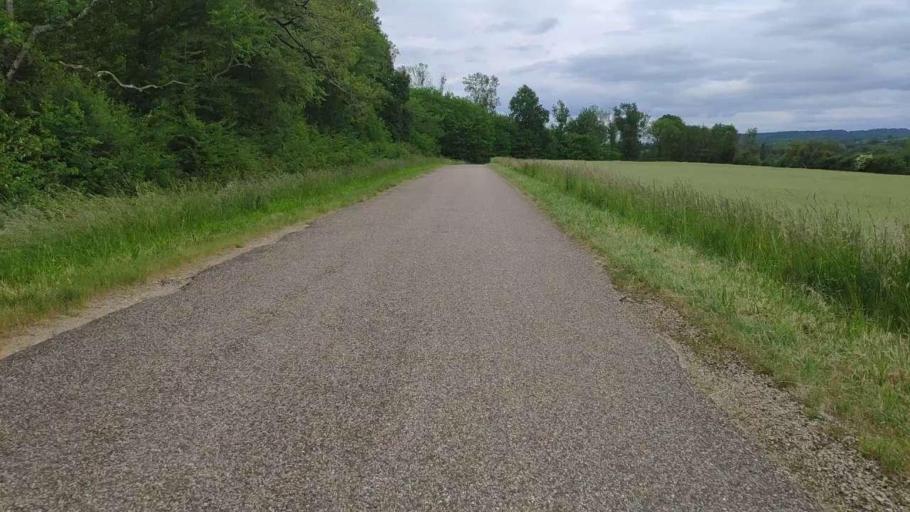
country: FR
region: Franche-Comte
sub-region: Departement du Jura
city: Bletterans
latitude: 46.7684
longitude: 5.5171
